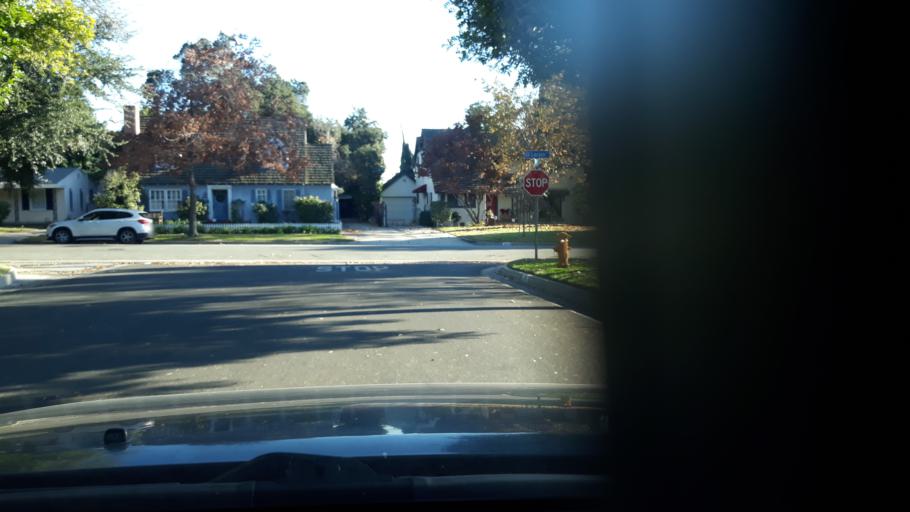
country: US
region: California
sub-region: Los Angeles County
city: San Marino
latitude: 34.1210
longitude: -118.0949
